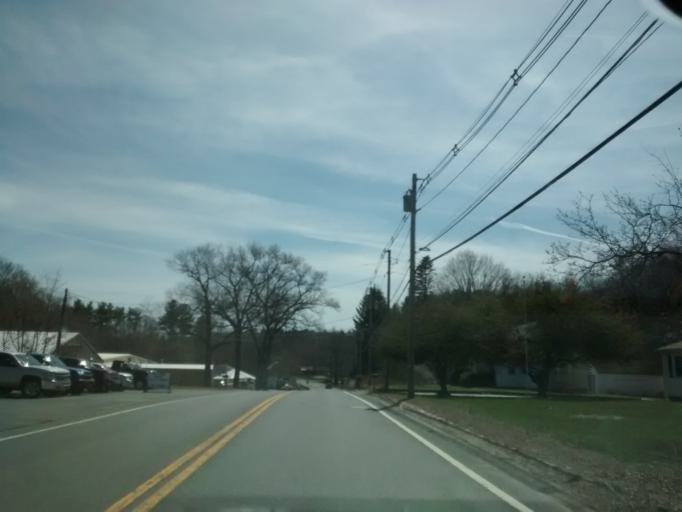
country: US
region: Massachusetts
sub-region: Worcester County
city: Northbridge
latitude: 42.1395
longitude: -71.6454
